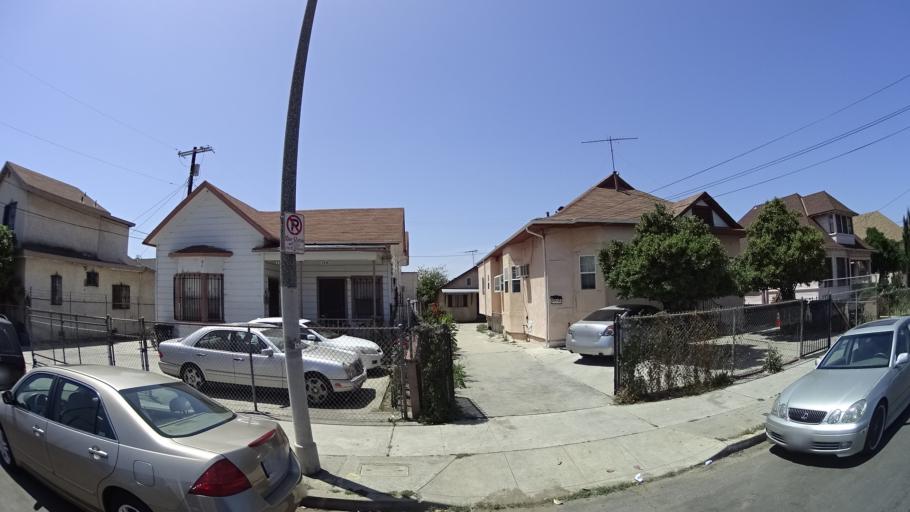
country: US
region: California
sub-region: Los Angeles County
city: Boyle Heights
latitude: 34.0727
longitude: -118.2078
